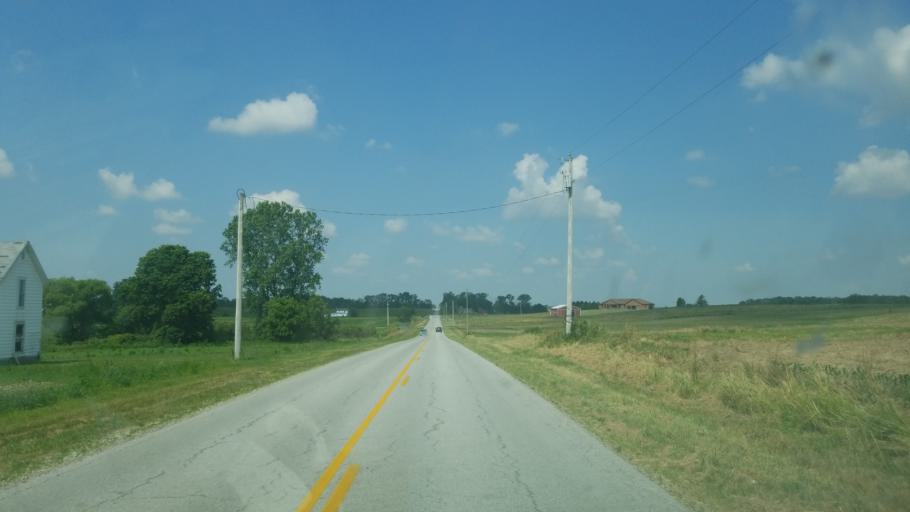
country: US
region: Ohio
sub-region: Auglaize County
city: Cridersville
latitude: 40.5709
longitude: -84.0877
